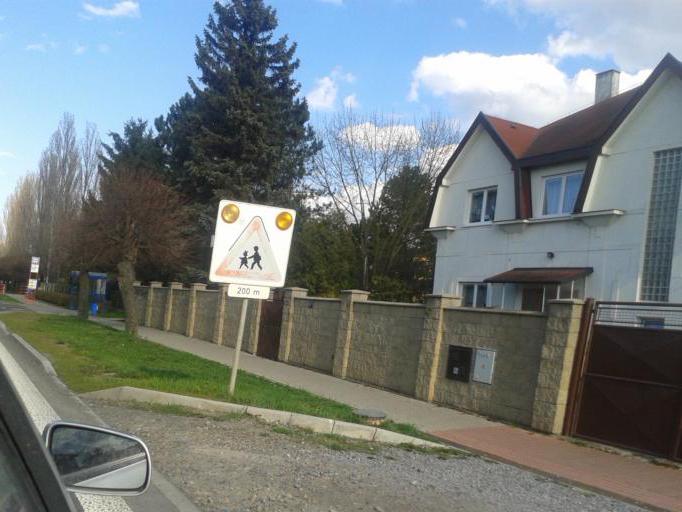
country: CZ
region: Central Bohemia
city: Rudna
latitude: 50.0298
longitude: 14.2209
